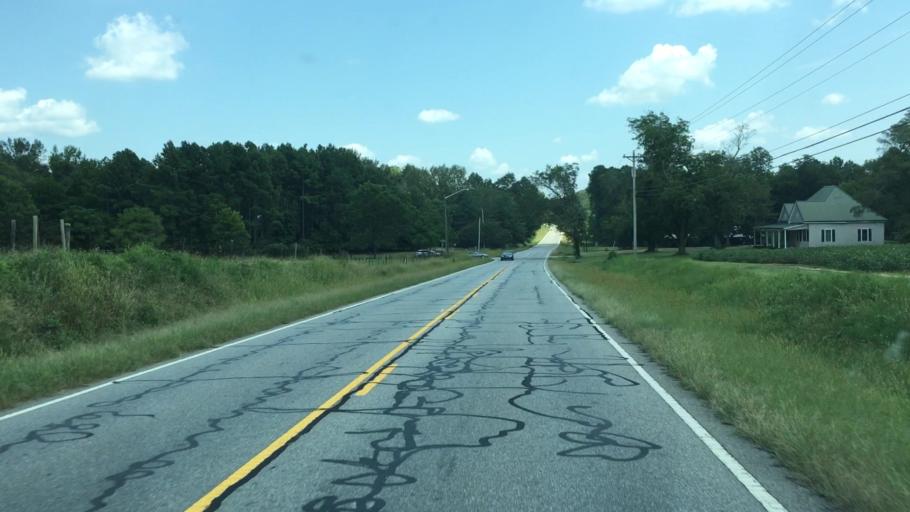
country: US
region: Georgia
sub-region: Oconee County
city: Watkinsville
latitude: 33.8691
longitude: -83.4941
